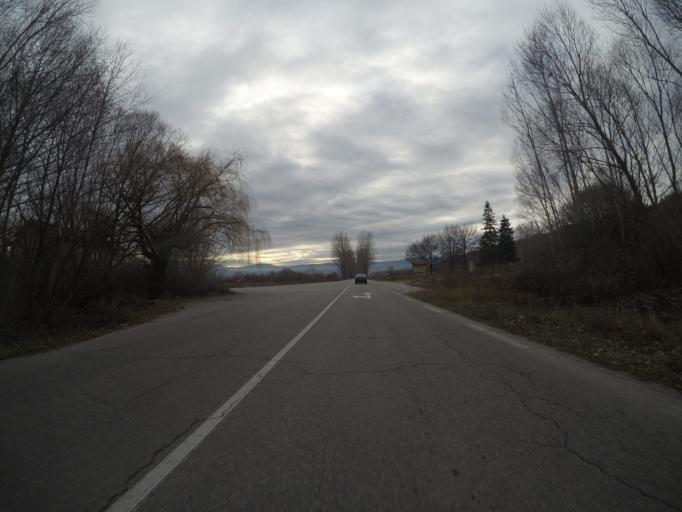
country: BG
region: Kyustendil
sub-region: Obshtina Kocherinovo
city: Kocherinovo
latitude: 42.1029
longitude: 23.0915
